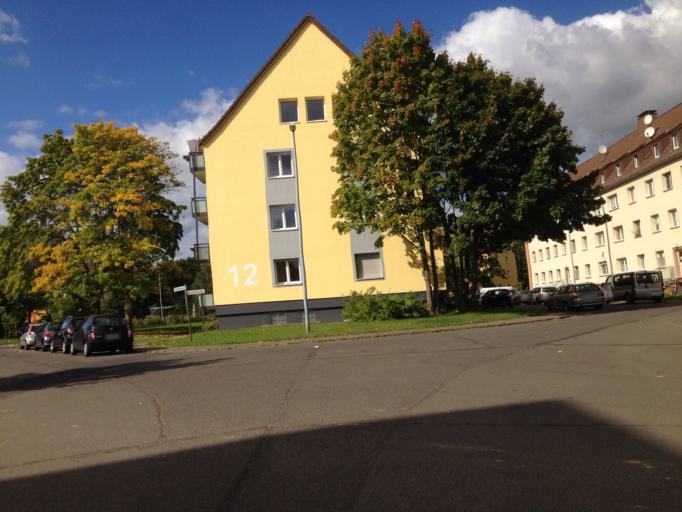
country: DE
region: Hesse
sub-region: Regierungsbezirk Giessen
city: Giessen
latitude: 50.5879
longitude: 8.7032
